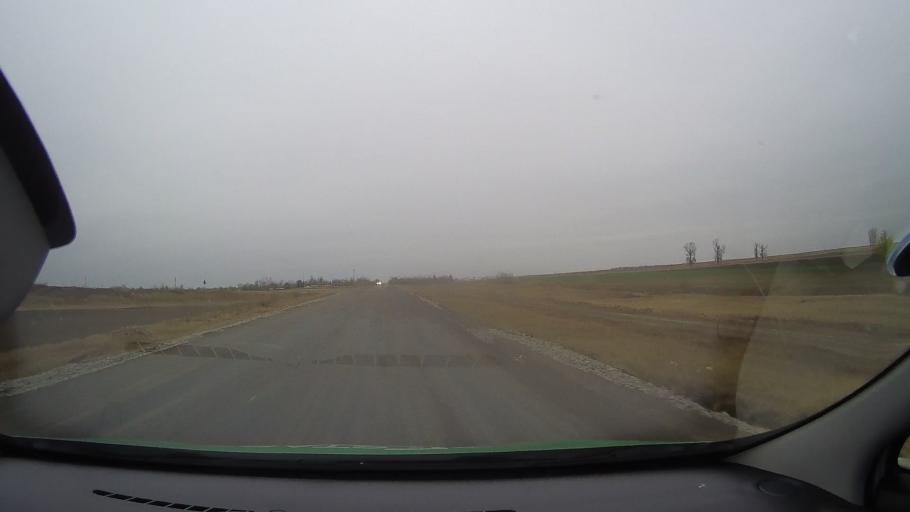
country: RO
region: Braila
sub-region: Comuna Baraganul
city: Baraganul
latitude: 44.8074
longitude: 27.5240
